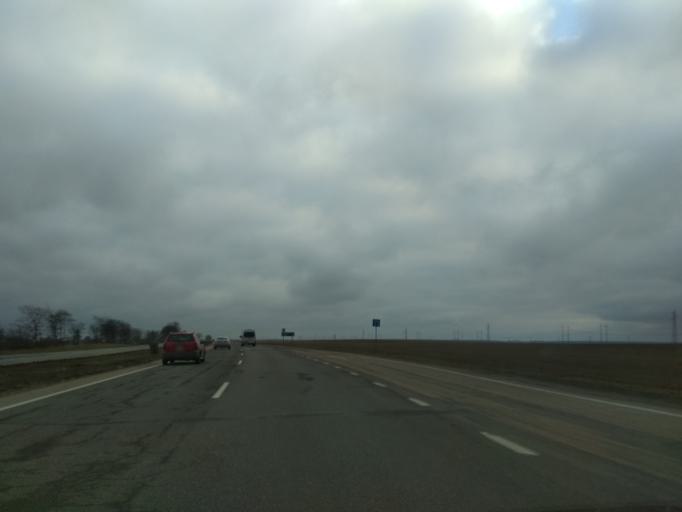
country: BY
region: Minsk
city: Dukora
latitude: 53.7028
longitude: 27.8811
